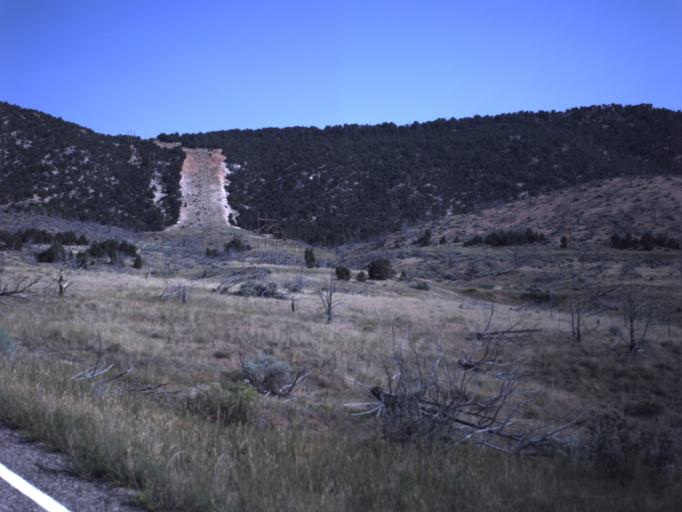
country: US
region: Utah
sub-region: Daggett County
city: Manila
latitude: 40.9492
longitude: -109.4436
